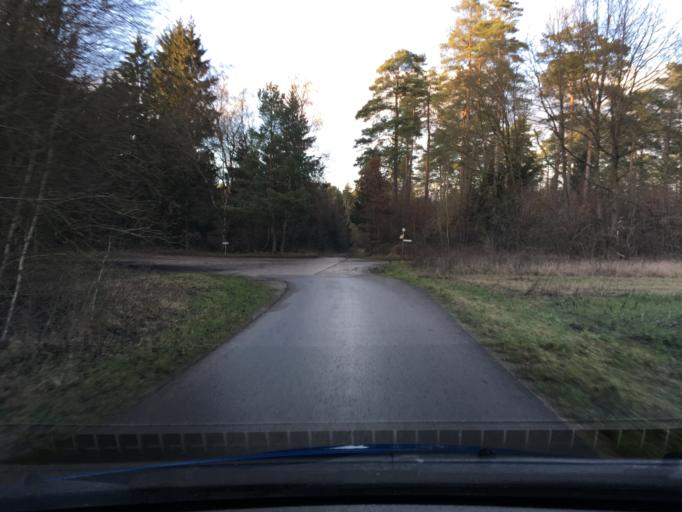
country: DE
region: Lower Saxony
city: Soderstorf
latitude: 53.1071
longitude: 10.1407
